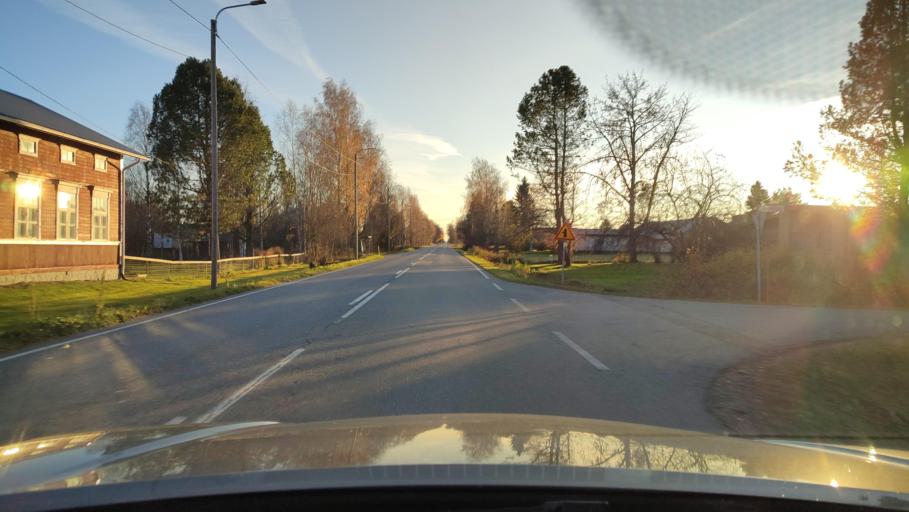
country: FI
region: Ostrobothnia
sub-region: Sydosterbotten
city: Naerpes
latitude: 62.5965
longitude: 21.4505
